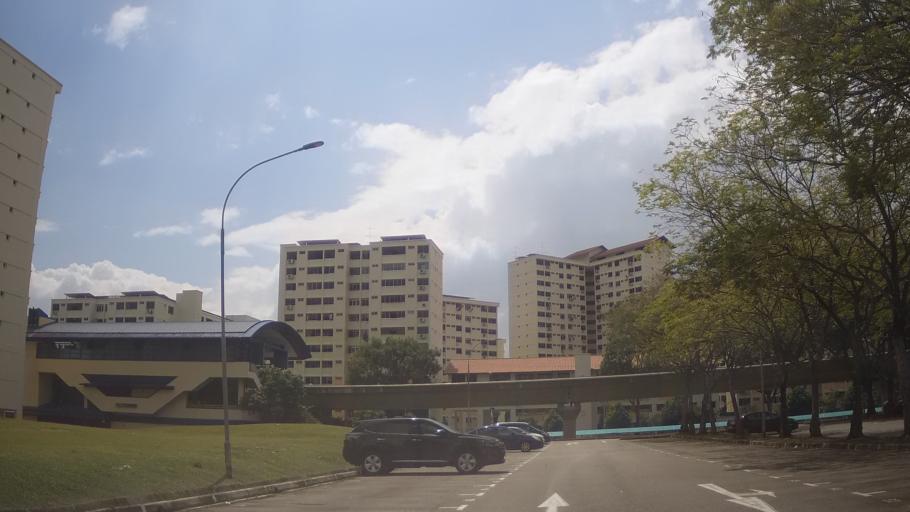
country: MY
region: Johor
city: Johor Bahru
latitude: 1.3805
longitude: 103.7734
